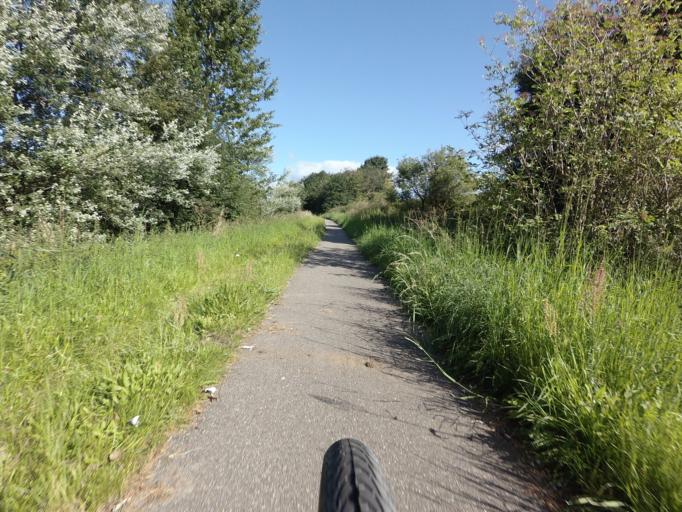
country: DK
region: Central Jutland
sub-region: Horsens Kommune
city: Horsens
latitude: 55.9483
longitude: 9.7853
